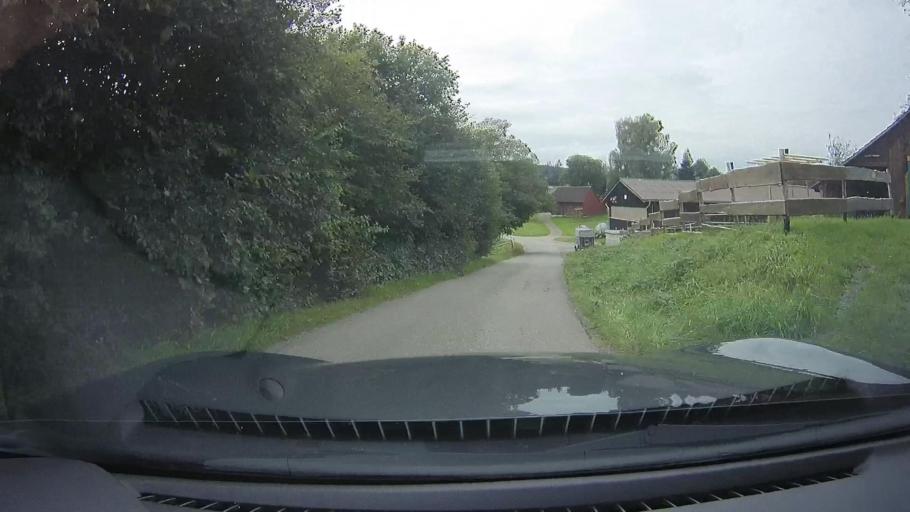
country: DE
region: Baden-Wuerttemberg
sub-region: Regierungsbezirk Stuttgart
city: Sulzbach an der Murr
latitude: 48.9865
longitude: 9.5057
